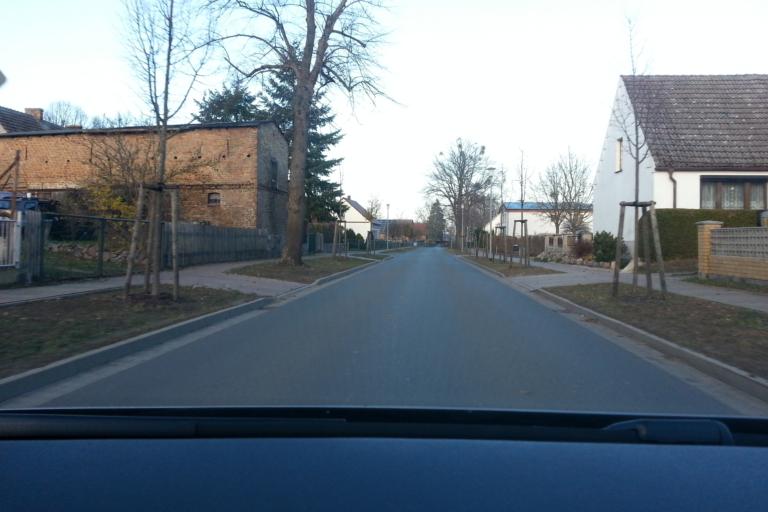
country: DE
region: Mecklenburg-Vorpommern
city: Ferdinandshof
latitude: 53.6434
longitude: 13.8605
